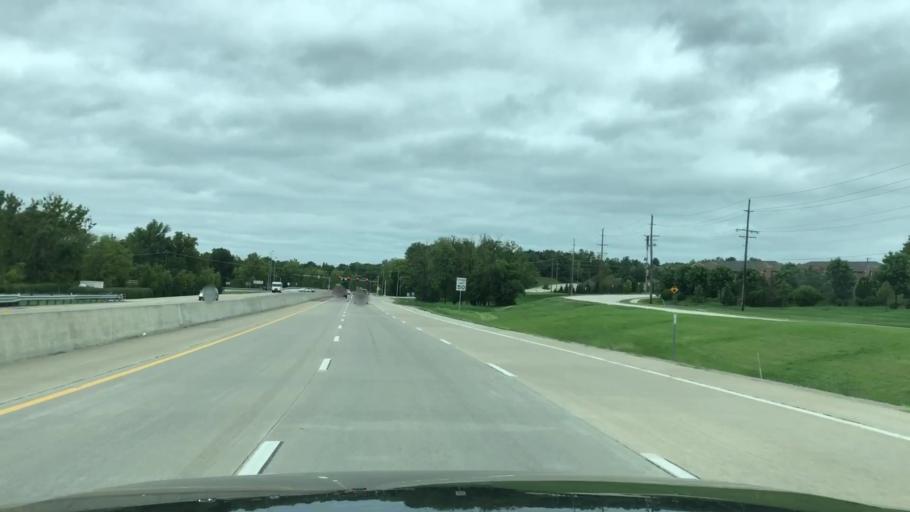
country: US
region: Missouri
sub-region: Saint Louis County
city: Manchester
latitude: 38.6561
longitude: -90.5069
